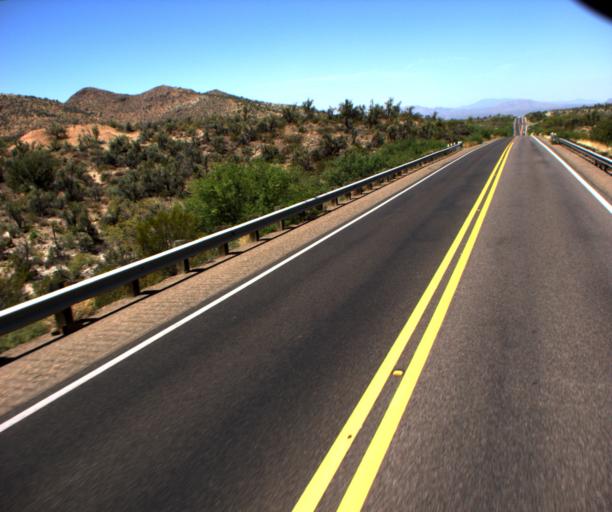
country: US
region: Arizona
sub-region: Gila County
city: Peridot
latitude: 33.2860
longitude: -110.3639
